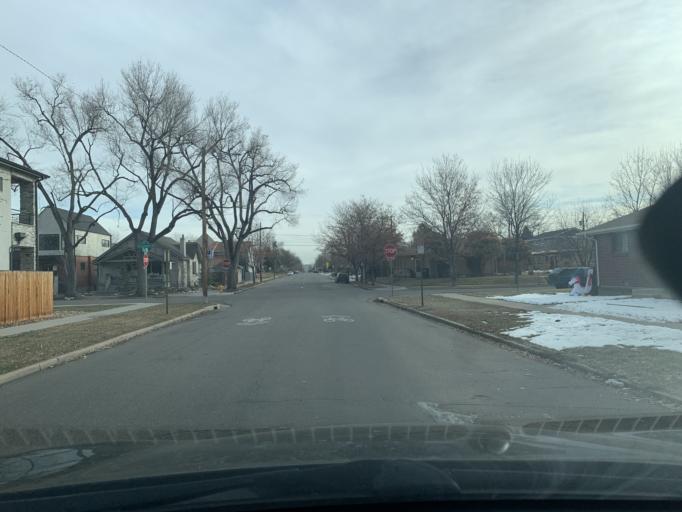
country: US
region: Colorado
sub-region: Jefferson County
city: Edgewater
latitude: 39.7512
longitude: -105.0410
